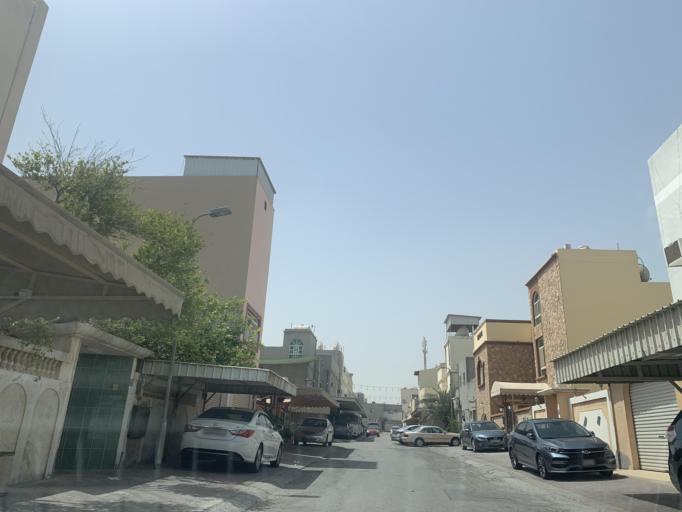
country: BH
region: Northern
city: Madinat `Isa
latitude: 26.1509
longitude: 50.5255
